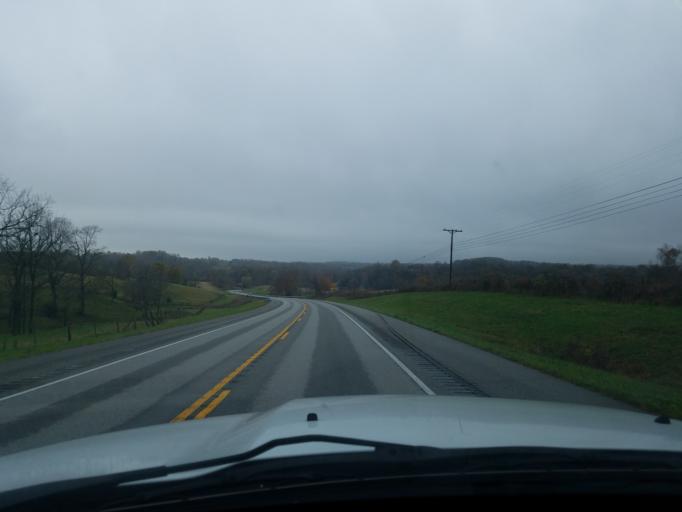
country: US
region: Kentucky
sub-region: Taylor County
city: Campbellsville
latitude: 37.3935
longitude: -85.4603
